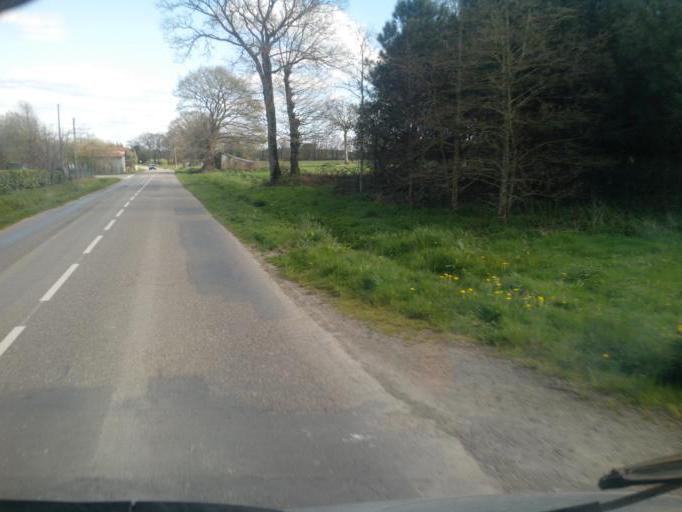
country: FR
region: Brittany
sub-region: Departement d'Ille-et-Vilaine
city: Plelan-le-Grand
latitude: 47.9926
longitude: -2.0704
